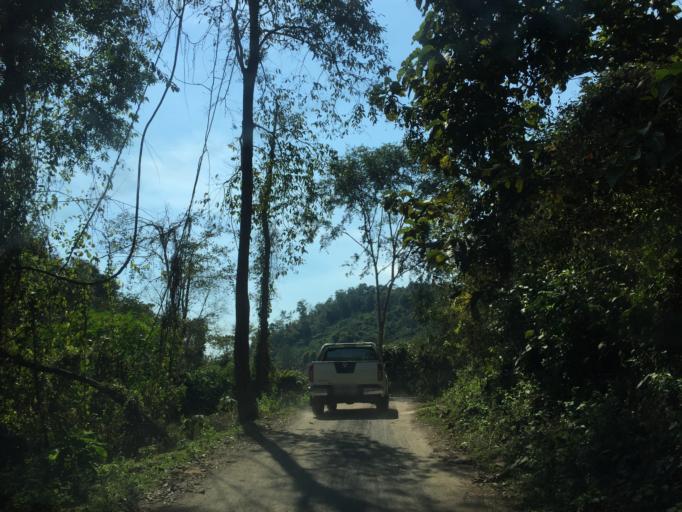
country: TH
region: Chiang Mai
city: Samoeng
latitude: 19.0098
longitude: 98.7310
